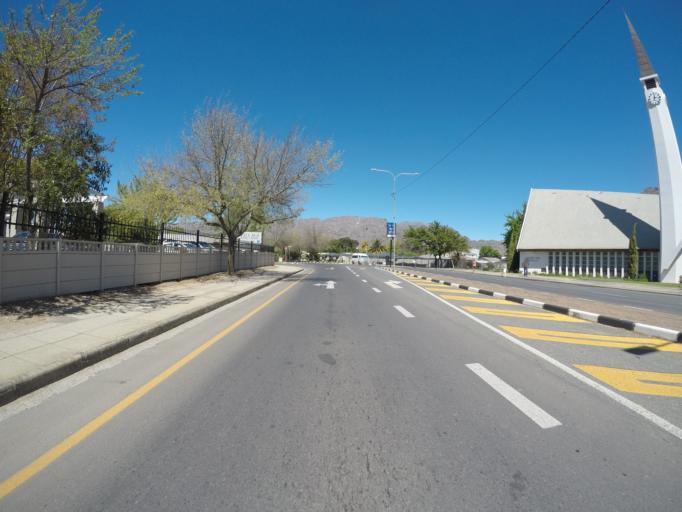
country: ZA
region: Western Cape
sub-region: Cape Winelands District Municipality
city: Ceres
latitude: -33.3654
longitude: 19.3098
